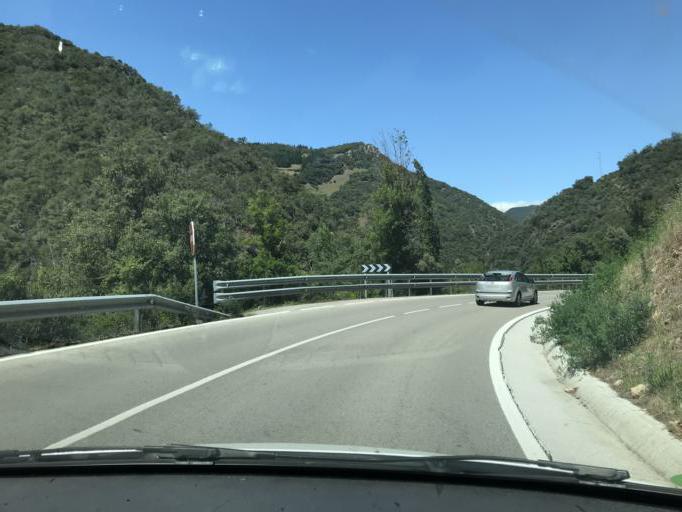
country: ES
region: Cantabria
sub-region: Provincia de Cantabria
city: Cabezon de Liebana
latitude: 43.1072
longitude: -4.5735
